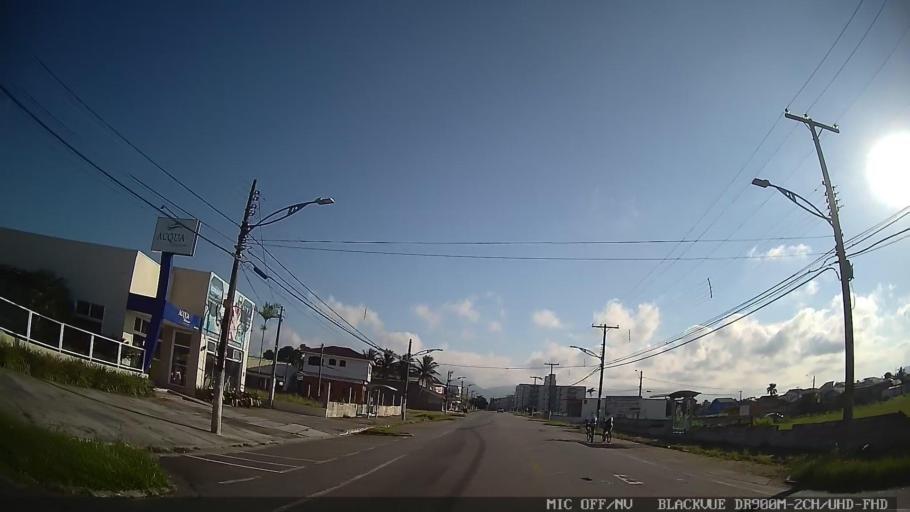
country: BR
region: Sao Paulo
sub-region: Peruibe
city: Peruibe
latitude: -24.2890
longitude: -46.9598
